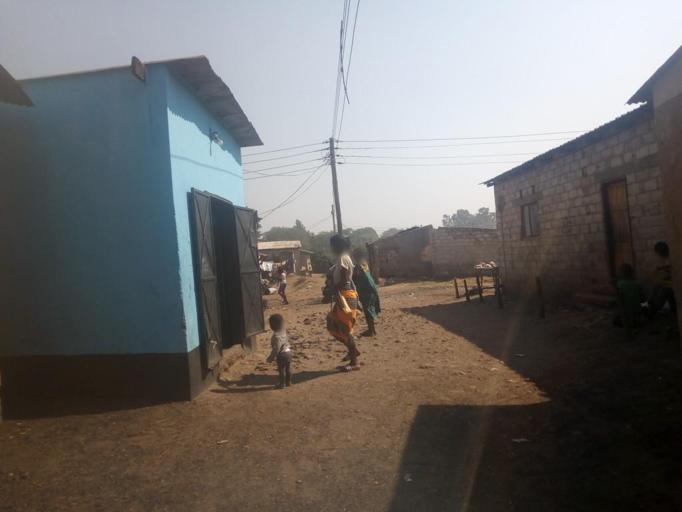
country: ZM
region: Lusaka
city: Lusaka
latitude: -15.4053
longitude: 28.3647
